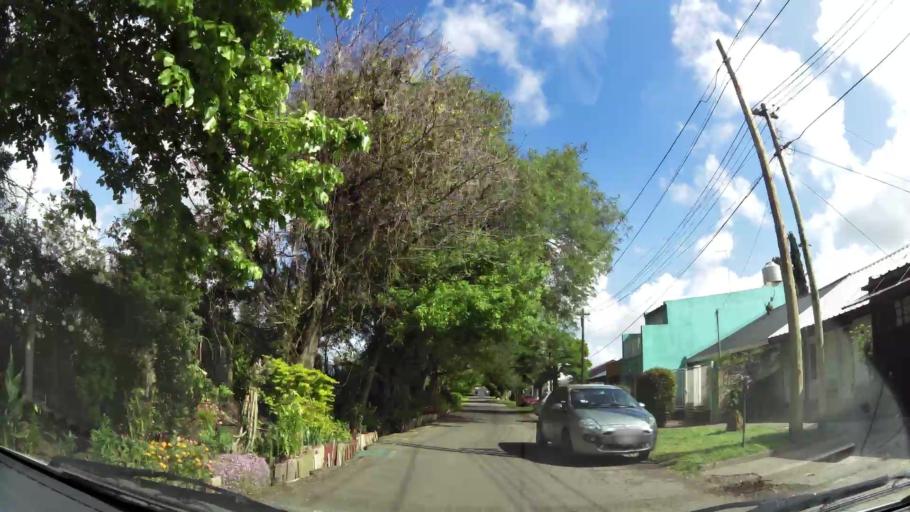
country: AR
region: Buenos Aires
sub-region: Partido de Quilmes
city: Quilmes
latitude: -34.7996
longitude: -58.1594
